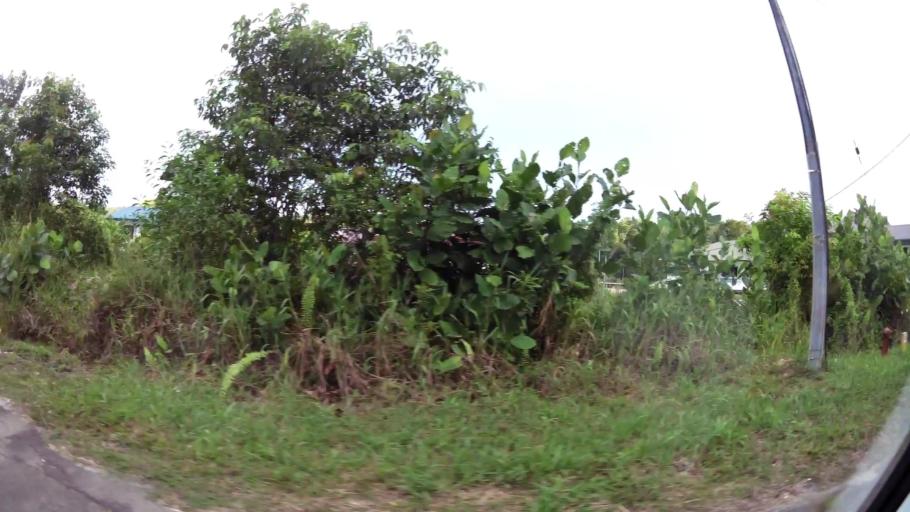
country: BN
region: Brunei and Muara
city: Bandar Seri Begawan
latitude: 4.9112
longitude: 115.0004
